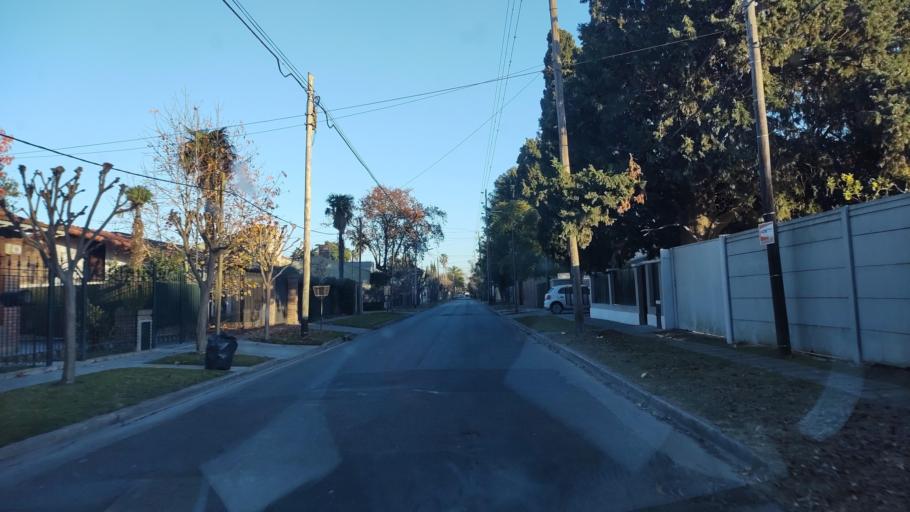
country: AR
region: Buenos Aires
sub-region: Partido de La Plata
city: La Plata
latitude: -34.8900
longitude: -58.0303
